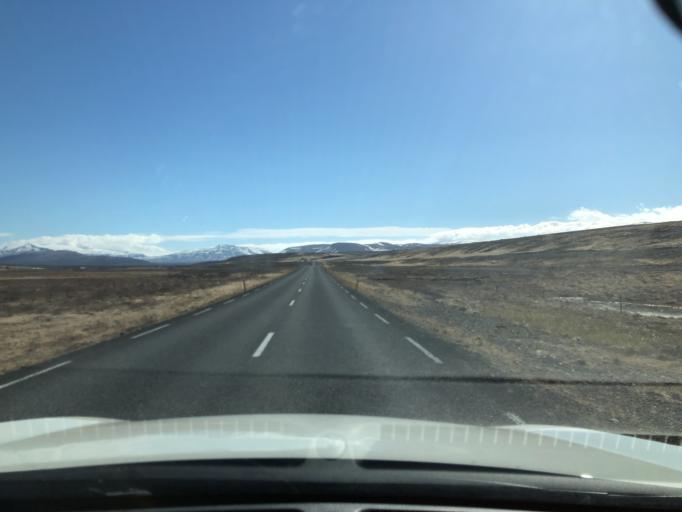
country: IS
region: South
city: Hveragerdi
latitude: 64.7003
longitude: -21.0853
